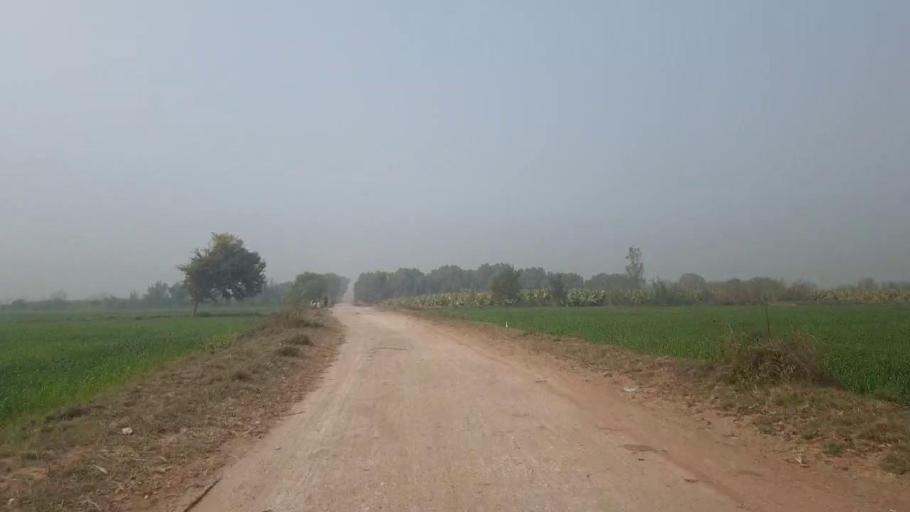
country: PK
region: Sindh
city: Bhit Shah
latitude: 25.8066
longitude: 68.5604
